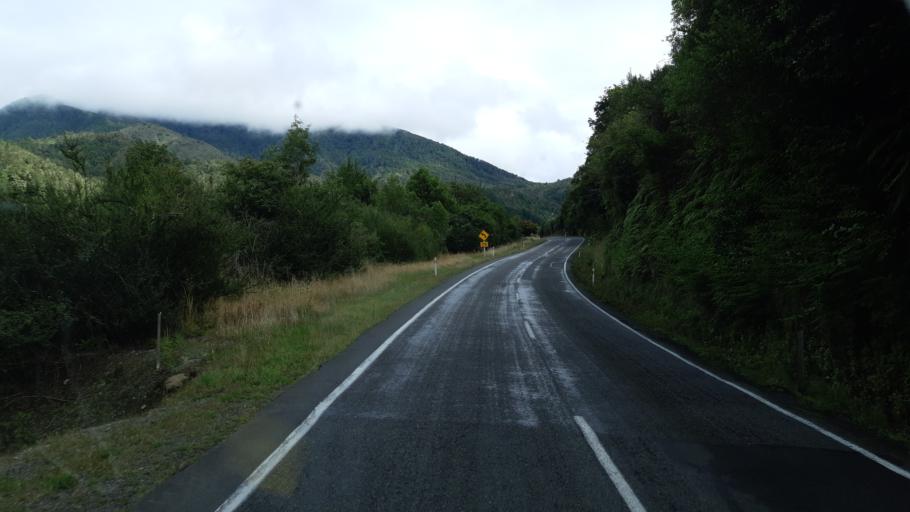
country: NZ
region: West Coast
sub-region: Buller District
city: Westport
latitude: -41.8108
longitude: 172.2276
